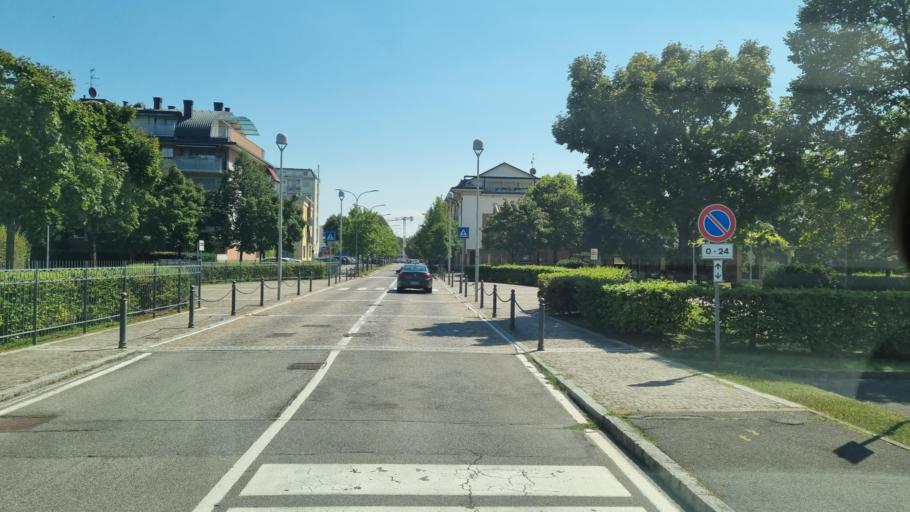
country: IT
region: Lombardy
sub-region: Provincia di Bergamo
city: Azzano San Paolo
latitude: 45.6638
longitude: 9.6763
